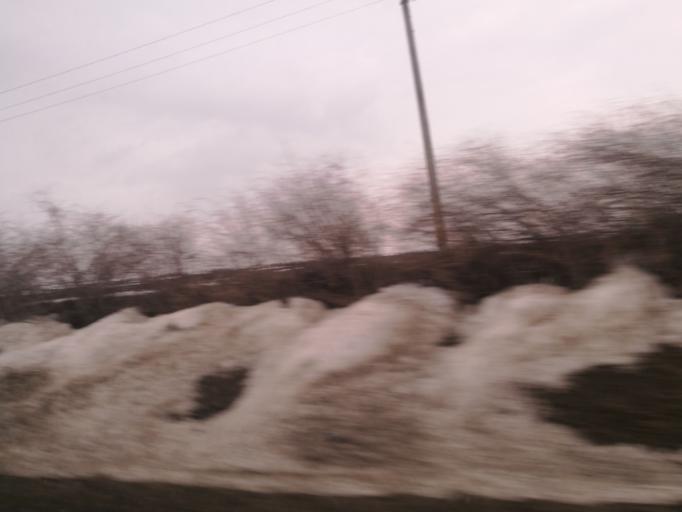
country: RO
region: Iasi
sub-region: Comuna Targu Frumos
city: Targu Frumos
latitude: 47.2056
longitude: 26.9850
